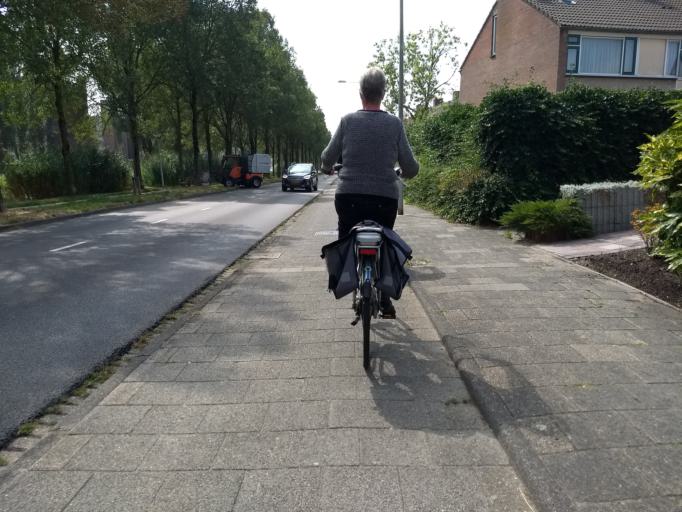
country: NL
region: South Holland
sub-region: Gemeente Papendrecht
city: Papendrecht
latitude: 51.8321
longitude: 4.6797
